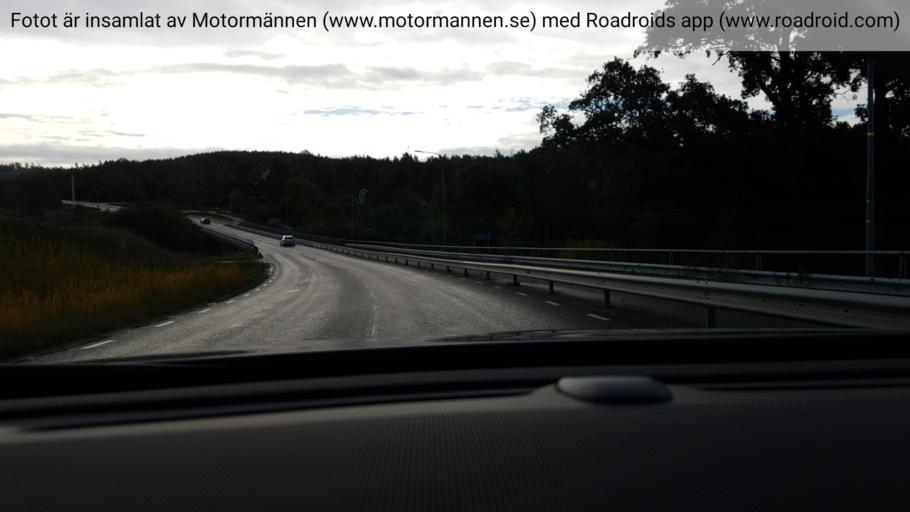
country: SE
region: Vaestra Goetaland
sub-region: Marks Kommun
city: Kinna
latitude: 57.4831
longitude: 12.6491
